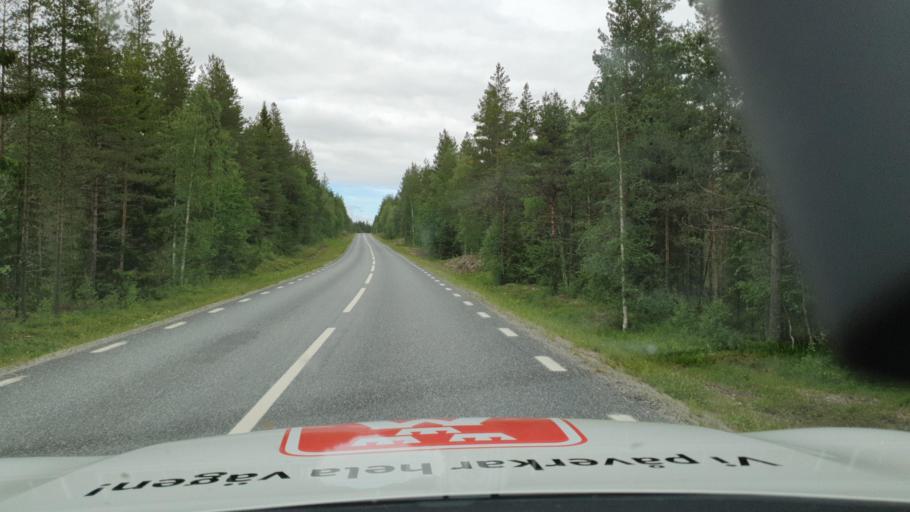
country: SE
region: Vaesterbotten
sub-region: Asele Kommun
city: Insjon
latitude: 64.2366
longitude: 17.5503
